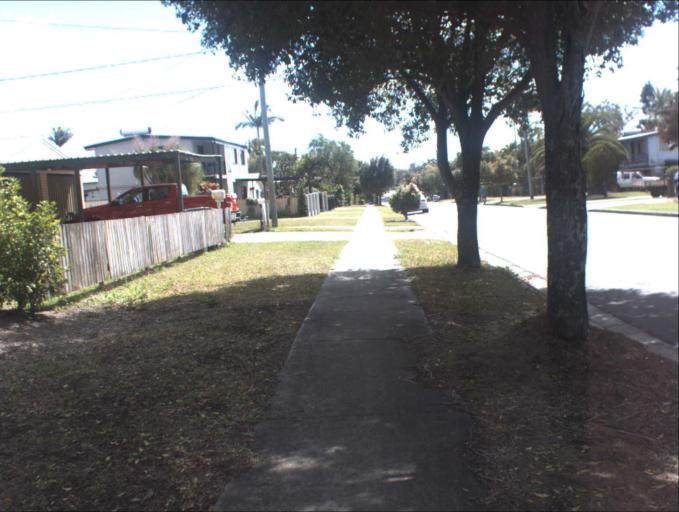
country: AU
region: Queensland
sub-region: Logan
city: Waterford West
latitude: -27.6737
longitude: 153.1055
